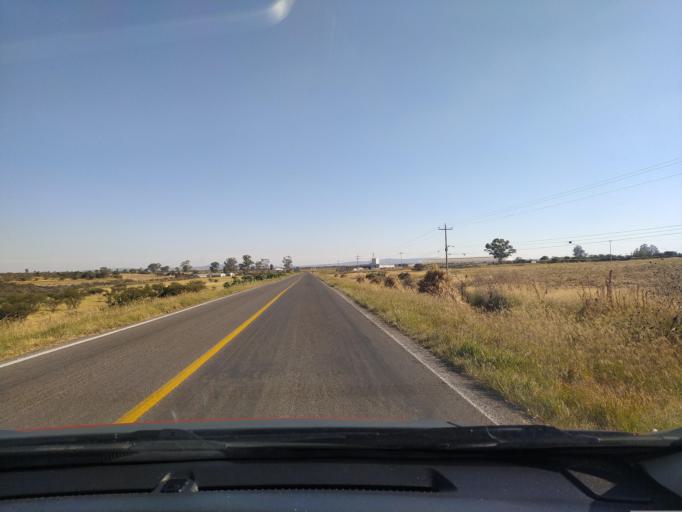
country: MX
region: Jalisco
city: Valle de Guadalupe
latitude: 21.0282
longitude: -102.5504
